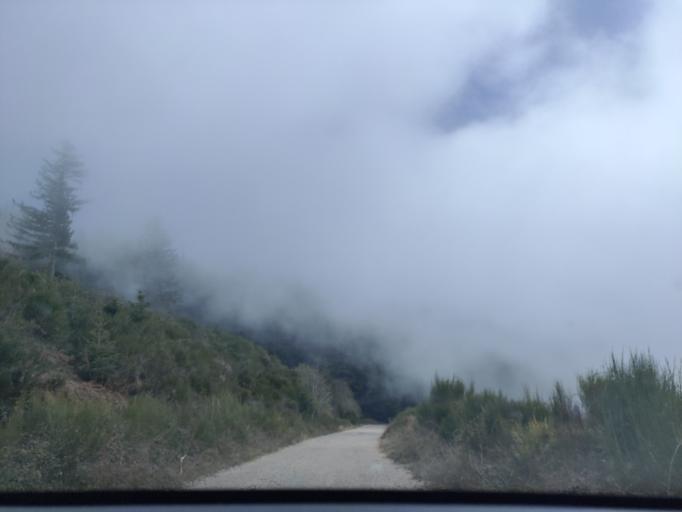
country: ES
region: Catalonia
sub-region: Provincia de Barcelona
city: Fogars de Montclus
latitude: 41.7591
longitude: 2.4564
